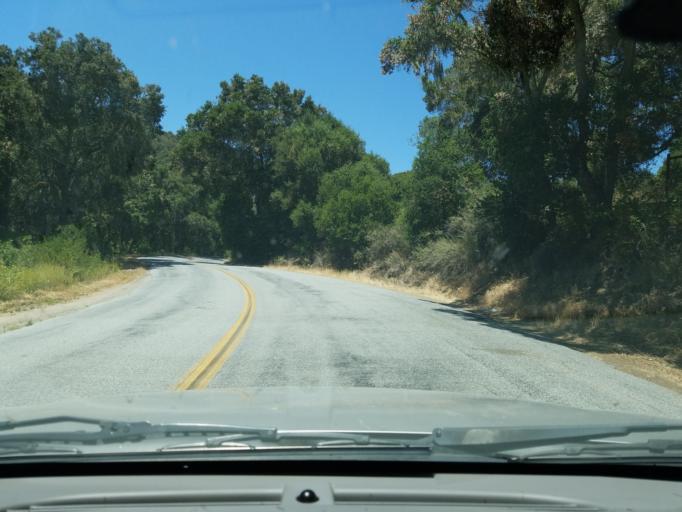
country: US
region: California
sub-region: Monterey County
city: Carmel Valley Village
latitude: 36.4544
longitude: -121.7015
